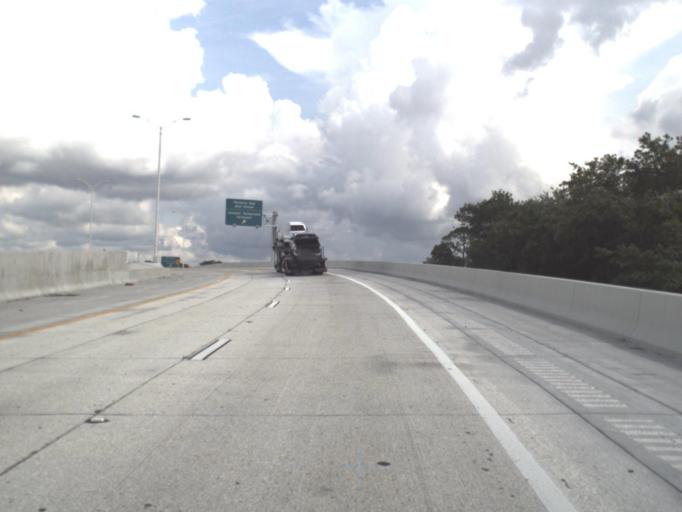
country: US
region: Florida
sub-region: Duval County
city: Jacksonville
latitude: 30.3534
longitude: -81.6368
